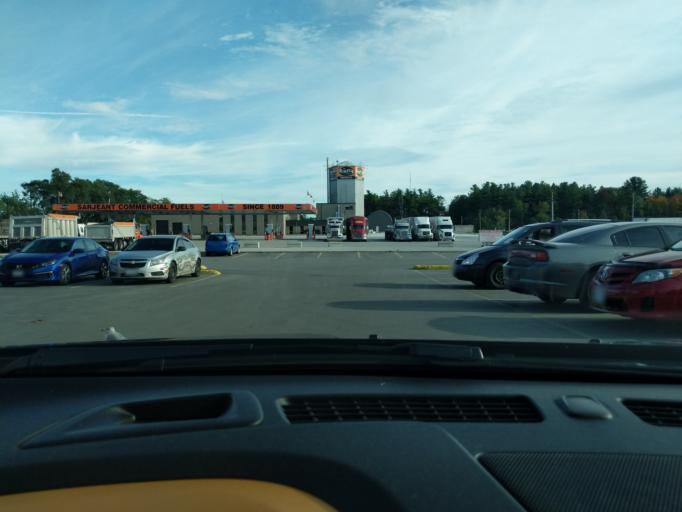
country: CA
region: Ontario
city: Barrie
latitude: 44.3771
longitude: -79.7156
